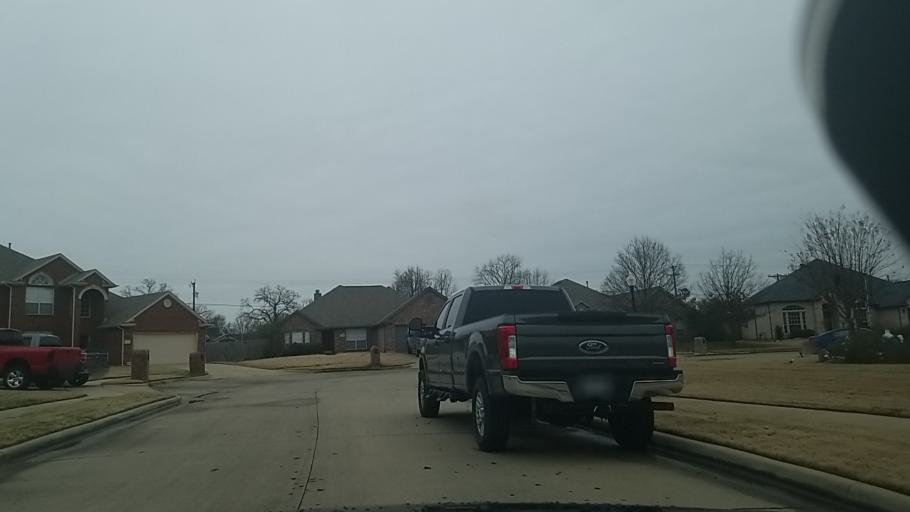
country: US
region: Texas
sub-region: Denton County
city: Corinth
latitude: 33.1551
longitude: -97.0695
